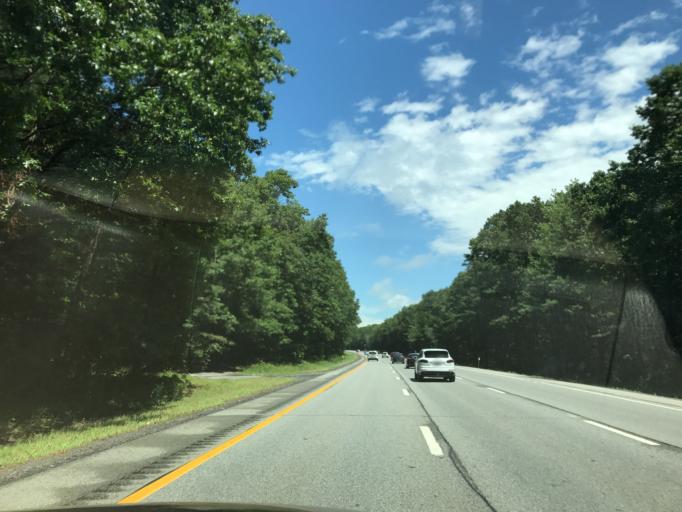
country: US
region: New York
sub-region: Saratoga County
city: Saratoga Springs
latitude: 43.1328
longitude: -73.7331
